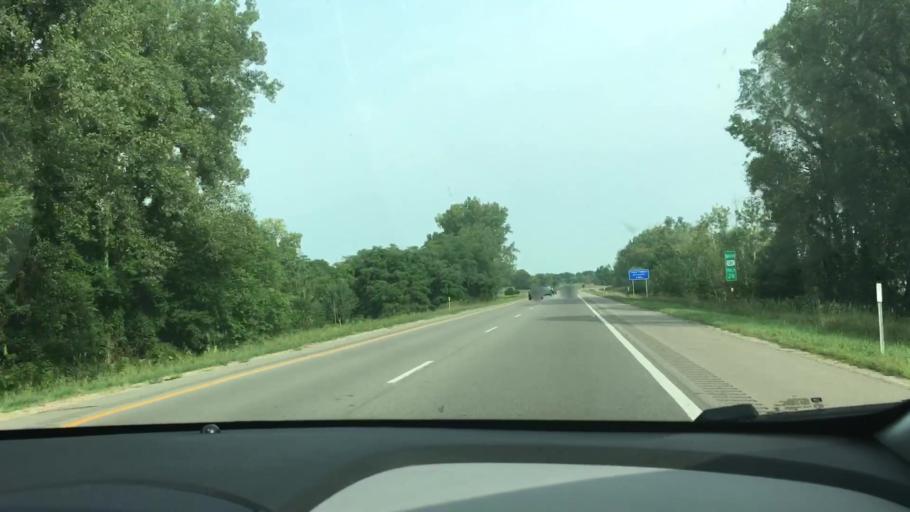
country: US
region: Michigan
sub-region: Kalamazoo County
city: Schoolcraft
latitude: 42.1508
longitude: -85.6402
